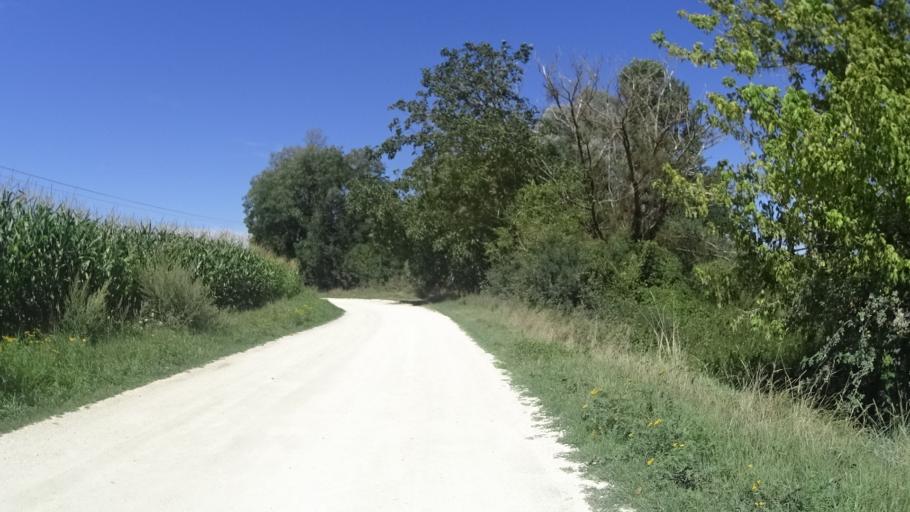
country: FR
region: Centre
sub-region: Departement du Loiret
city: Bonny-sur-Loire
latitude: 47.5424
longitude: 2.8387
